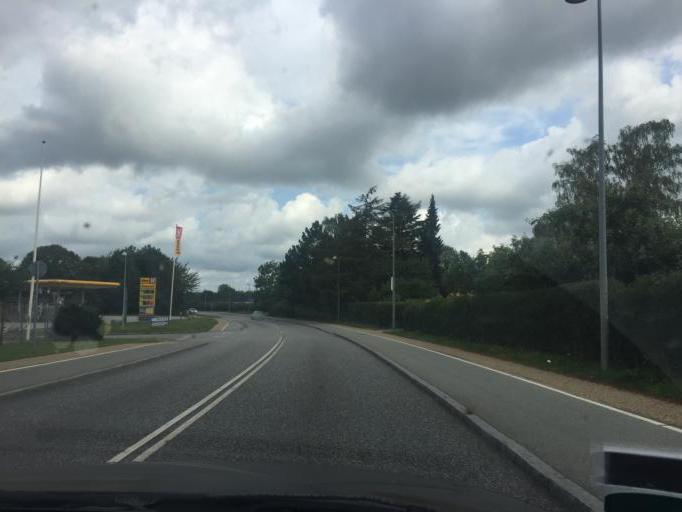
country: DK
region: Capital Region
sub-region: Allerod Kommune
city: Lillerod
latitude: 55.8869
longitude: 12.3550
